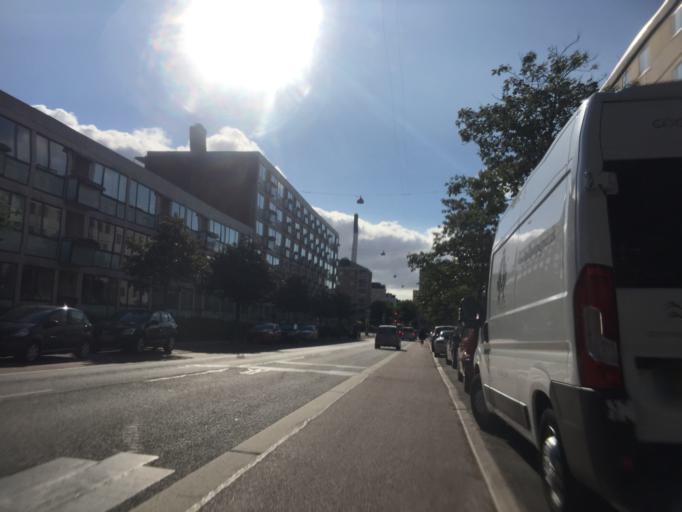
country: DK
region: Capital Region
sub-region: Kobenhavn
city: Vanlose
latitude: 55.6846
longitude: 12.5107
